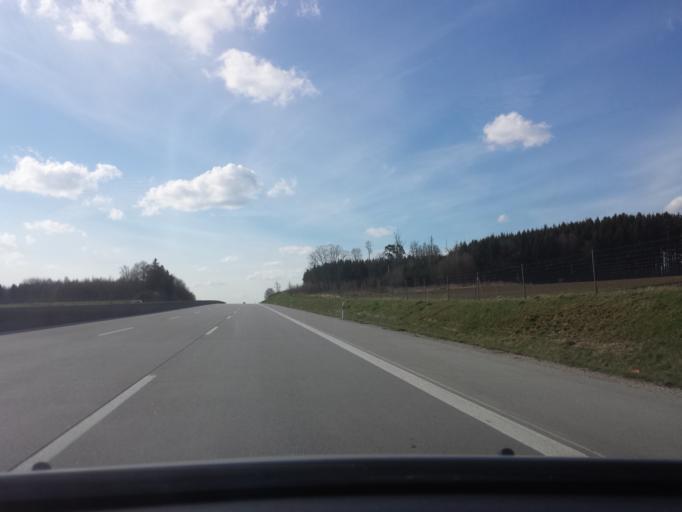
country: DE
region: Bavaria
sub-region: Upper Bavaria
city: Sulzemoos
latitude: 48.2898
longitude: 11.2488
